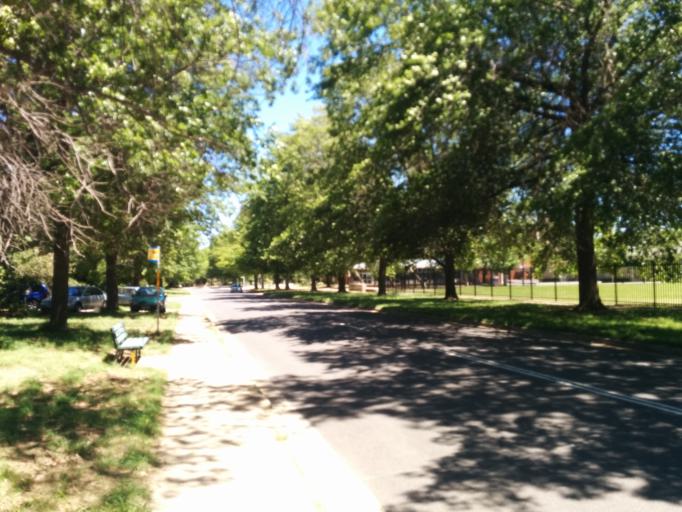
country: AU
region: Australian Capital Territory
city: Acton
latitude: -35.2509
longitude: 149.1313
